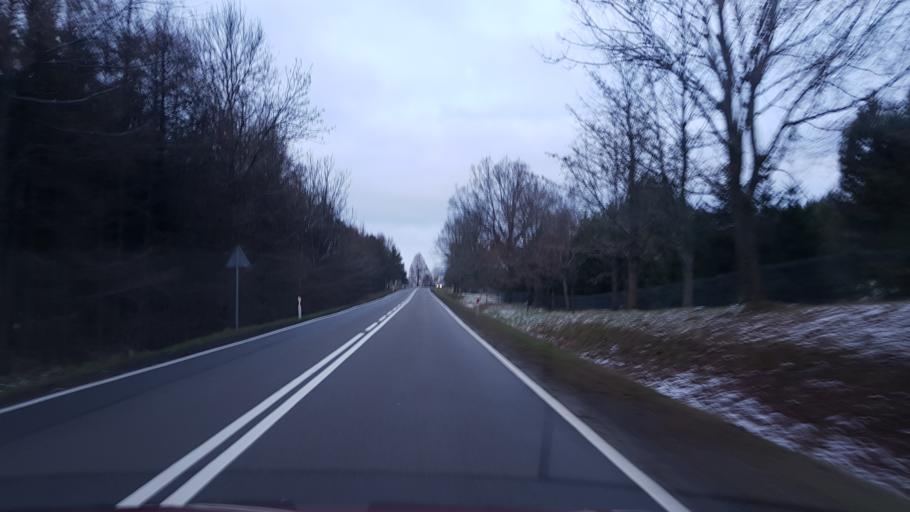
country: PL
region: Pomeranian Voivodeship
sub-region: Powiat bytowski
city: Tuchomie
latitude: 54.0733
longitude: 17.2859
